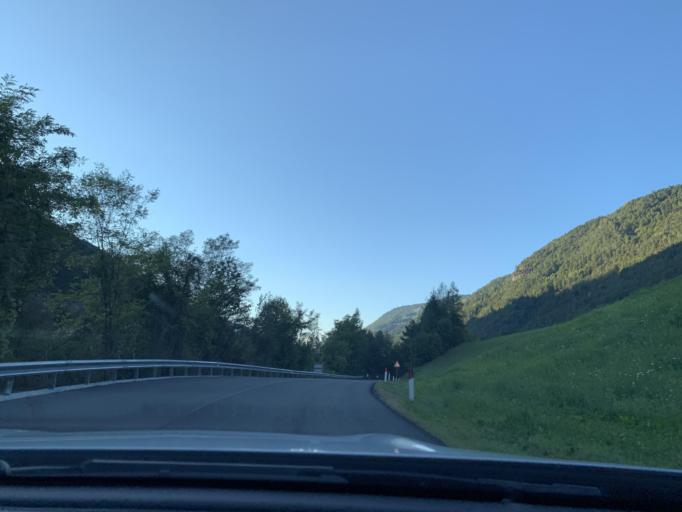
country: IT
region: Trentino-Alto Adige
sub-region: Bolzano
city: Nova Ponente
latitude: 46.4392
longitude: 11.4659
